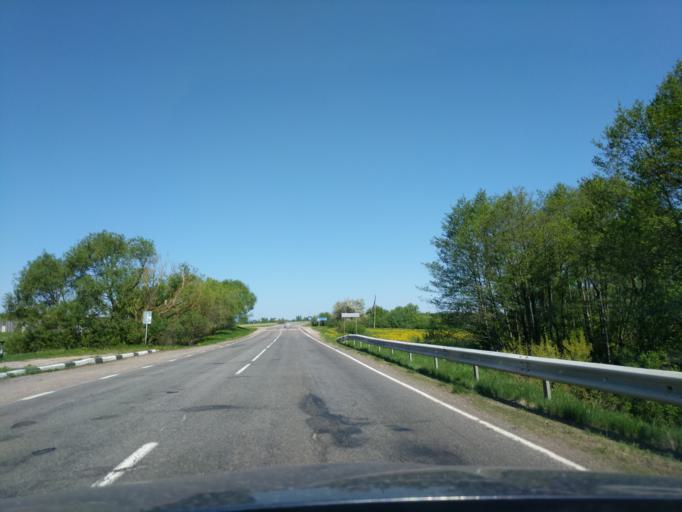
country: BY
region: Minsk
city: Il'ya
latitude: 54.2978
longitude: 27.4796
